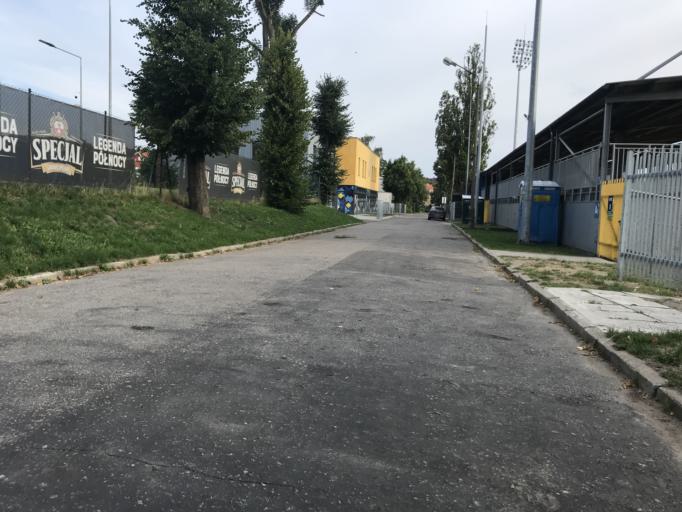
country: PL
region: Warmian-Masurian Voivodeship
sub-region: Powiat elblaski
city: Elblag
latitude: 54.1665
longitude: 19.4221
